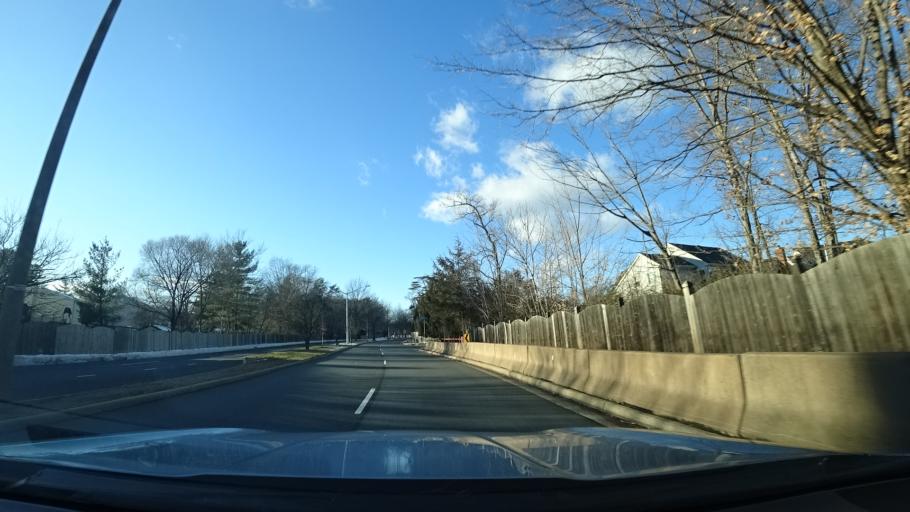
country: US
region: Virginia
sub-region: Fairfax County
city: Herndon
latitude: 38.9806
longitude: -77.3711
